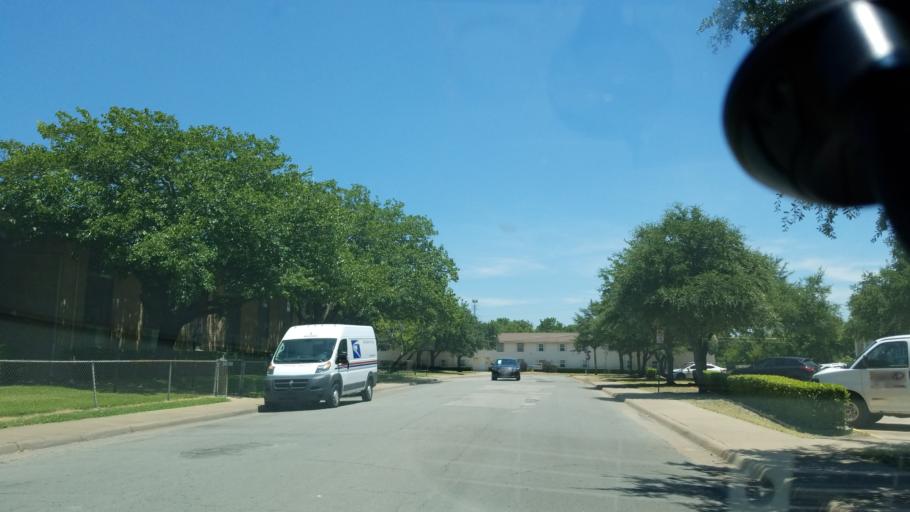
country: US
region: Texas
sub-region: Dallas County
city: Cockrell Hill
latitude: 32.7011
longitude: -96.8312
